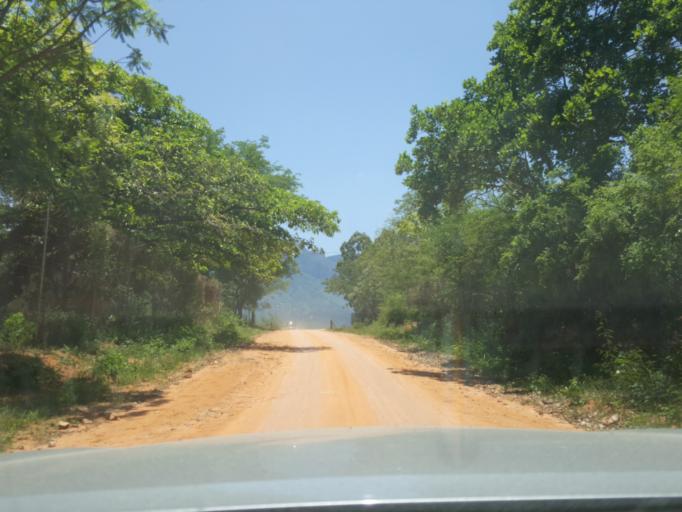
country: ZA
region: Limpopo
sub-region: Mopani District Municipality
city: Hoedspruit
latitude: -24.5922
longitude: 30.9410
